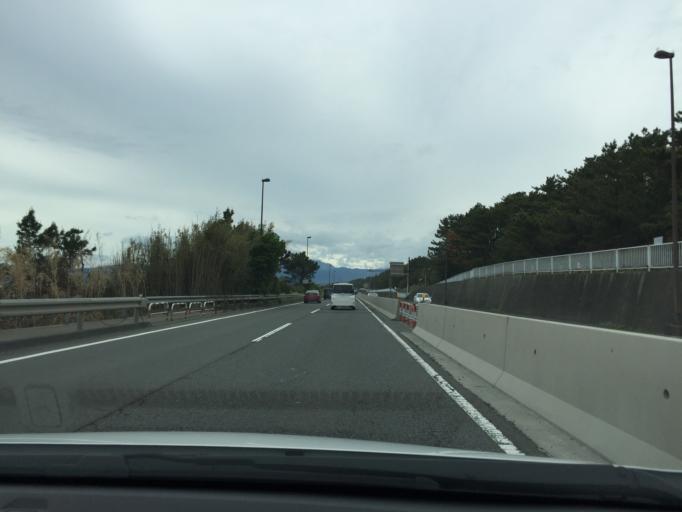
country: JP
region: Kanagawa
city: Oiso
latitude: 35.3058
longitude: 139.3074
